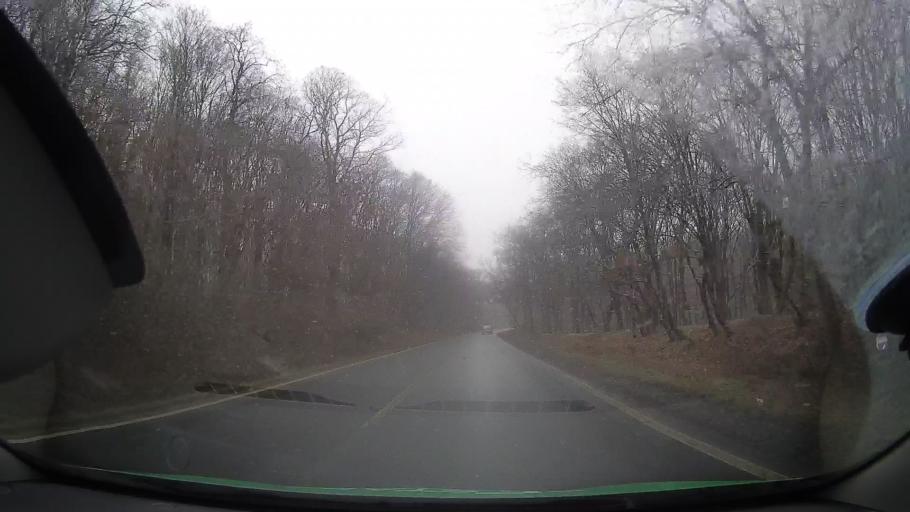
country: RO
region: Sibiu
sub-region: Comuna Blajel
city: Blajel
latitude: 46.1868
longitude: 24.3256
